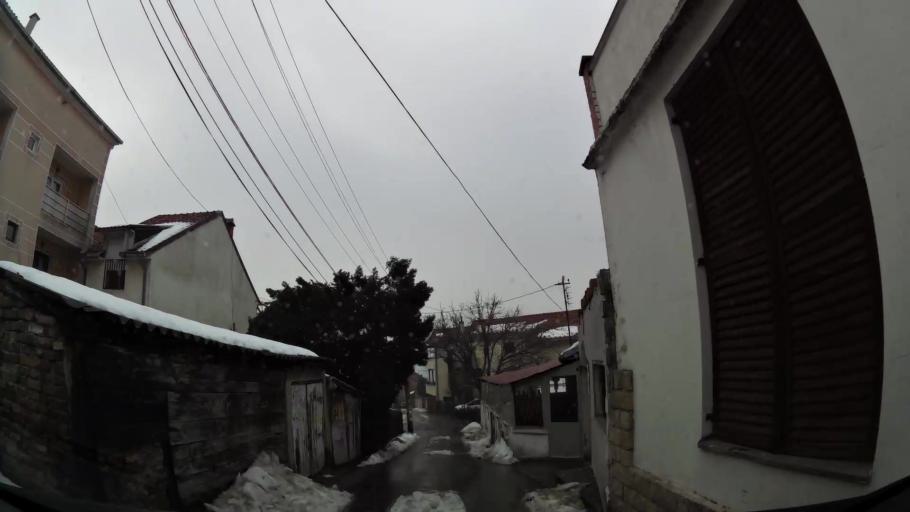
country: RS
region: Central Serbia
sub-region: Belgrade
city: Zvezdara
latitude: 44.7790
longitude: 20.5138
